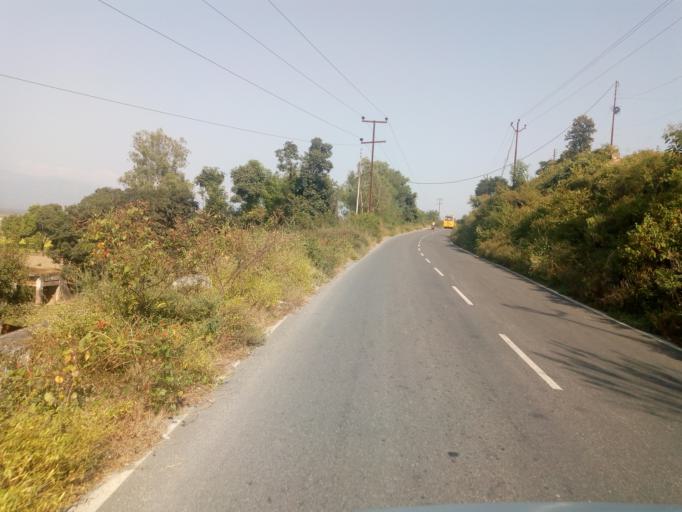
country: IN
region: Uttarakhand
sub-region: Dehradun
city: Harbatpur
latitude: 30.4414
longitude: 77.6860
